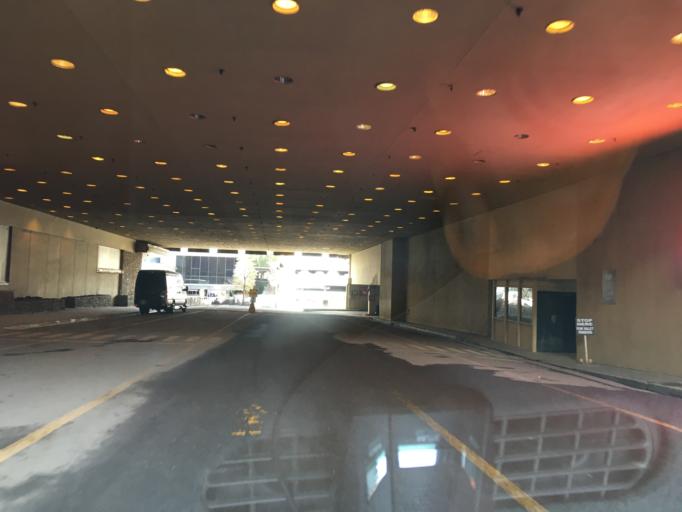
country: US
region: Nevada
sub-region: Douglas County
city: Kingsbury
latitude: 38.9601
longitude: -119.9404
